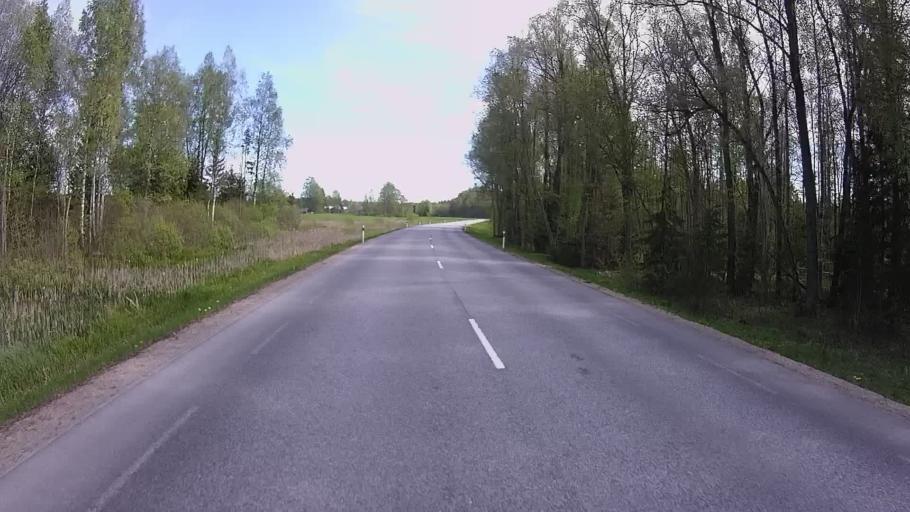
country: EE
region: Valgamaa
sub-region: Valga linn
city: Valga
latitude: 57.7111
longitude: 26.2268
